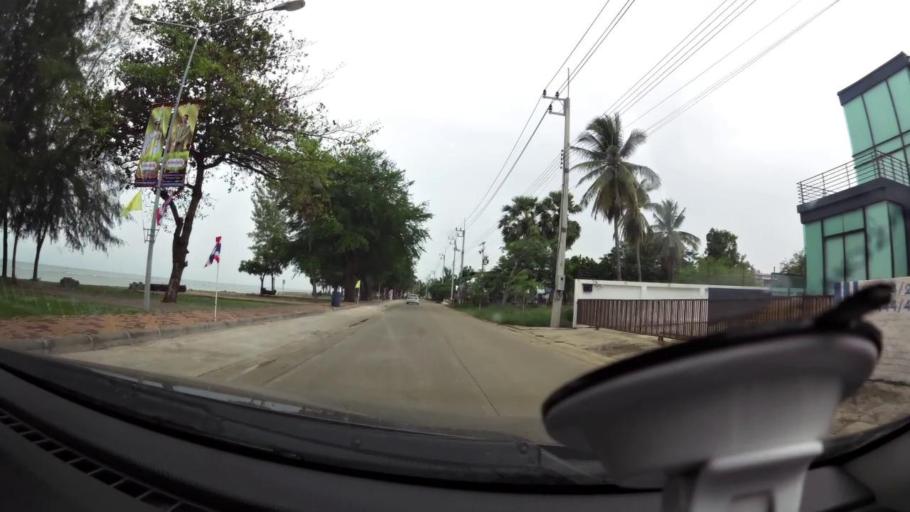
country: TH
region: Prachuap Khiri Khan
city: Pran Buri
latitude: 12.4000
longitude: 99.9944
